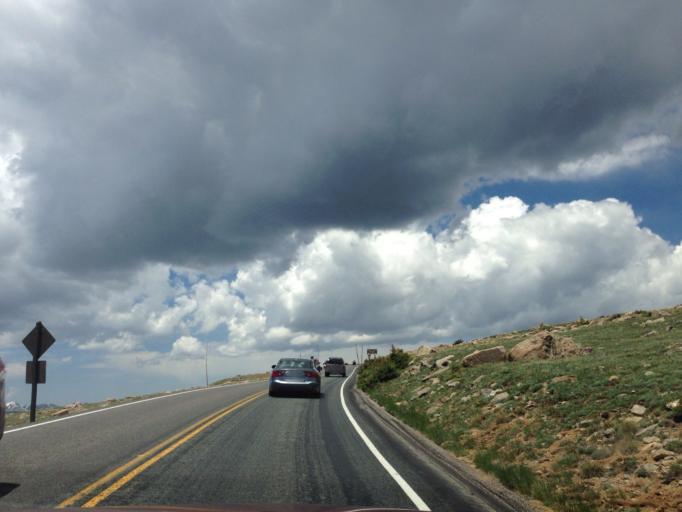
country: US
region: Colorado
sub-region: Larimer County
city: Estes Park
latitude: 40.3936
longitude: -105.7092
